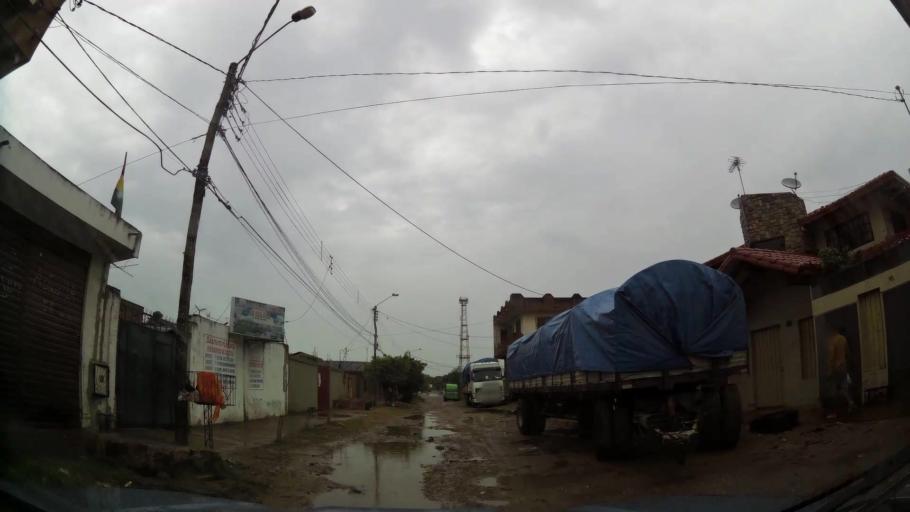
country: BO
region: Santa Cruz
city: Santa Cruz de la Sierra
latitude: -17.7983
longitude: -63.2169
